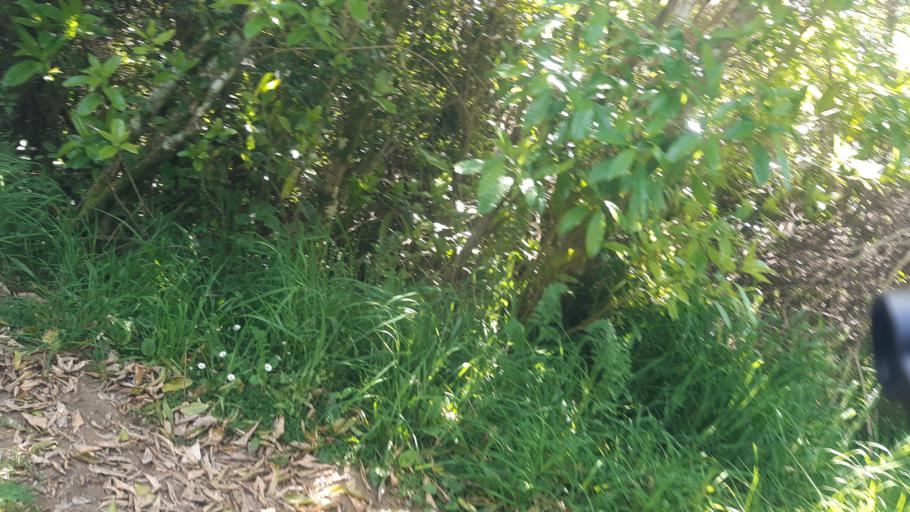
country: NZ
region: Marlborough
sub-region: Marlborough District
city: Picton
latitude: -41.2698
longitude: 174.0247
